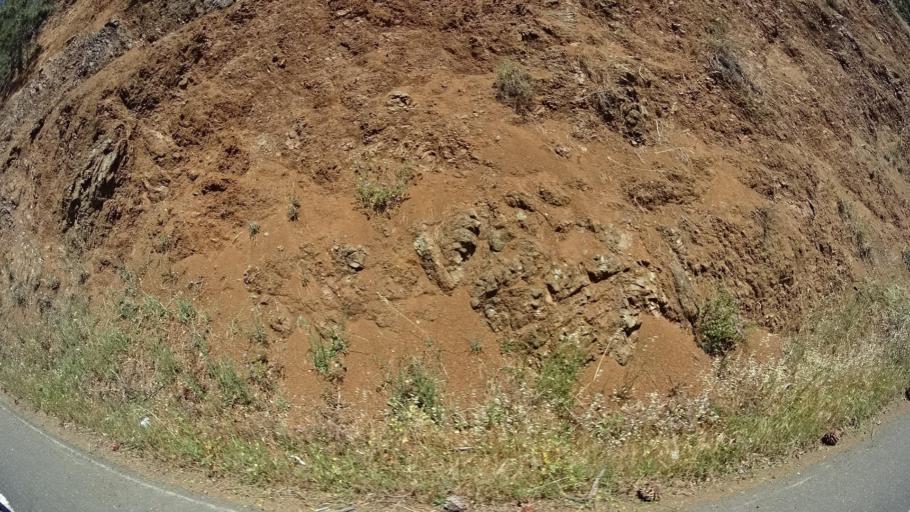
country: US
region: California
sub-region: Lake County
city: Clearlake Oaks
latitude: 39.0240
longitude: -122.7263
